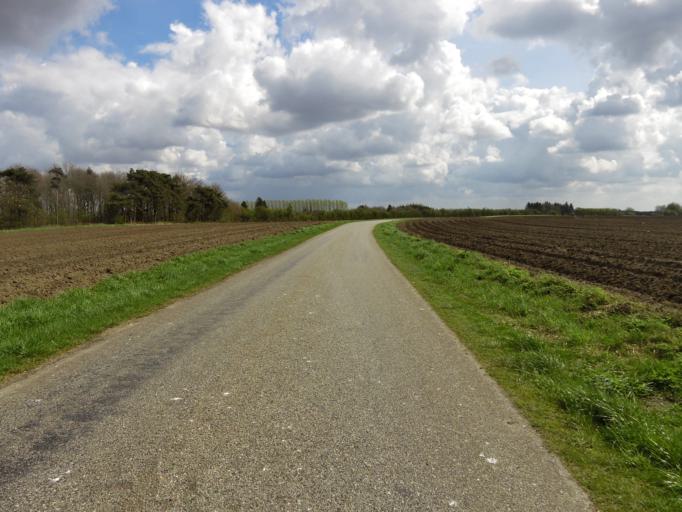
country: DK
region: South Denmark
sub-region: Tonder Kommune
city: Toftlund
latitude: 55.2091
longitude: 9.1605
